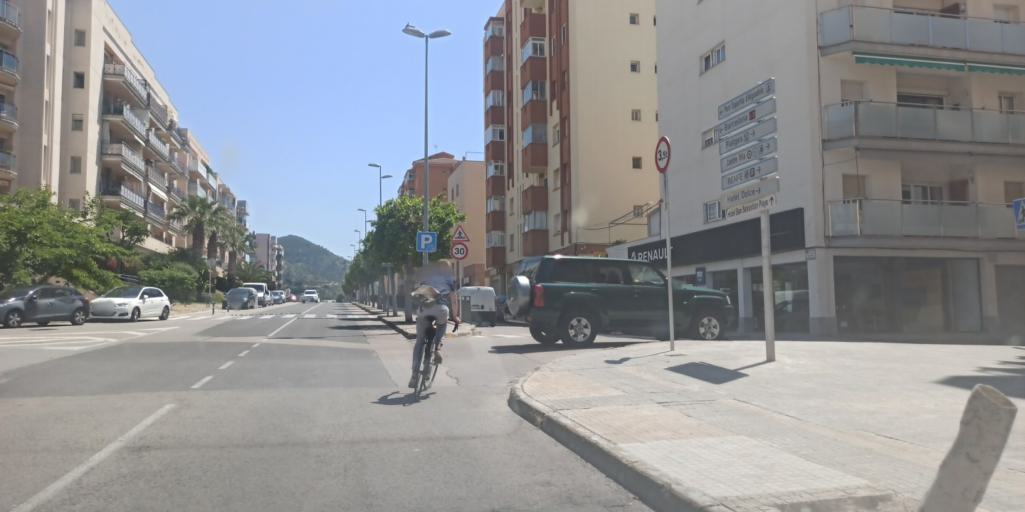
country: ES
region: Catalonia
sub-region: Provincia de Barcelona
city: Sitges
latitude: 41.2389
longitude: 1.8153
